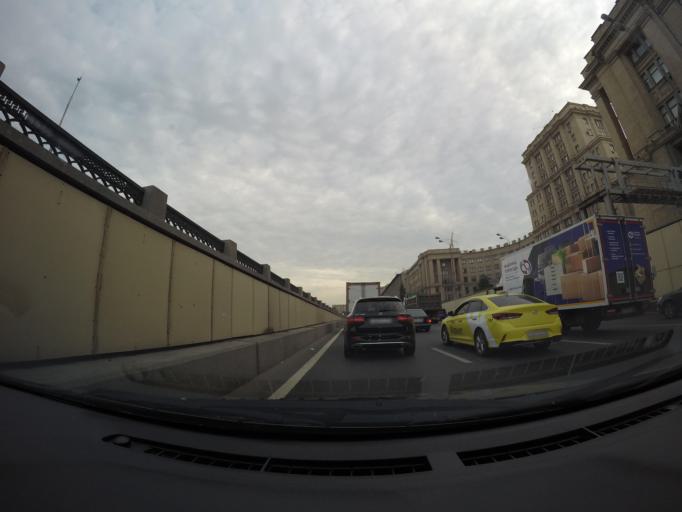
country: RU
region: Moscow
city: Lefortovo
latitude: 55.7663
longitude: 37.6872
